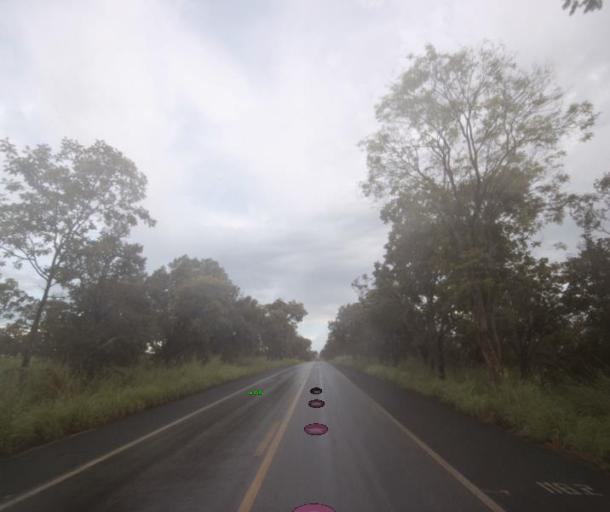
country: BR
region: Goias
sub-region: Porangatu
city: Porangatu
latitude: -13.8082
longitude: -49.0386
